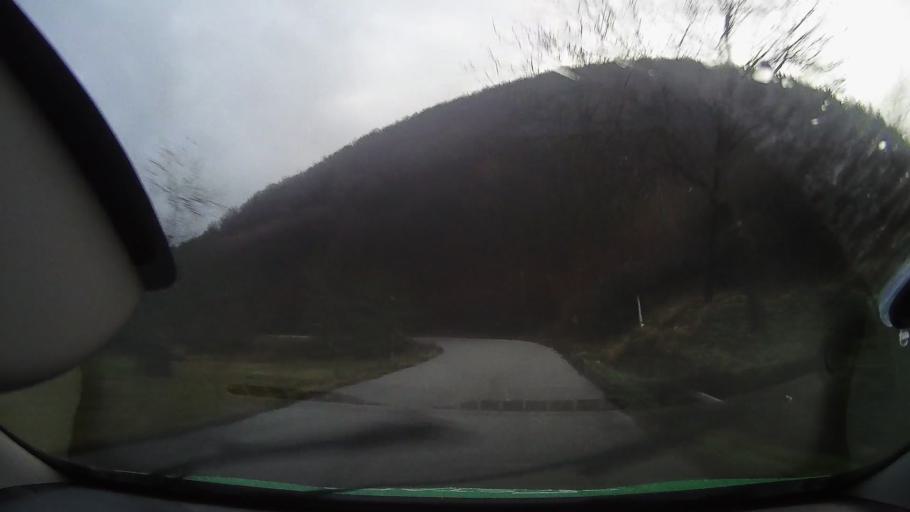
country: RO
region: Hunedoara
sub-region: Comuna Ribita
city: Ribita
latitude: 46.2770
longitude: 22.7409
